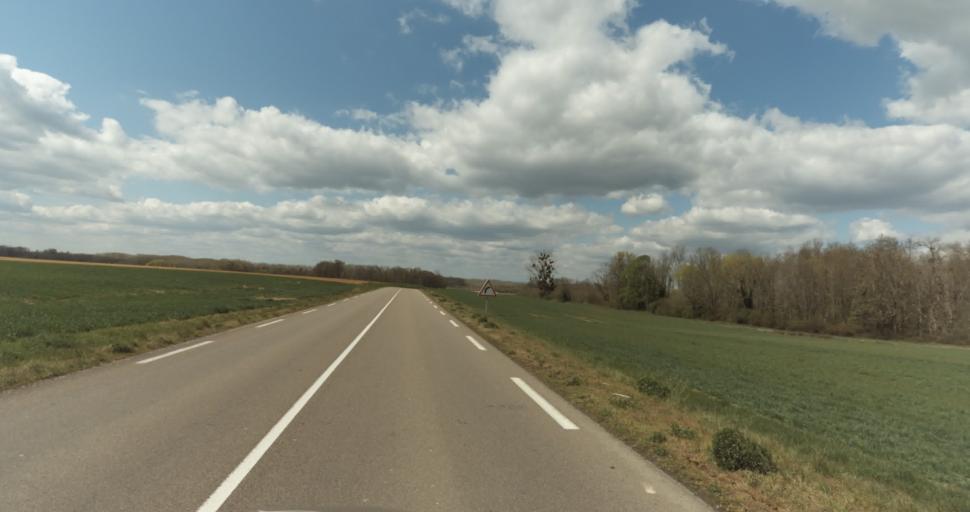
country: FR
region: Bourgogne
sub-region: Departement de la Cote-d'Or
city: Auxonne
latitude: 47.1619
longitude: 5.4075
